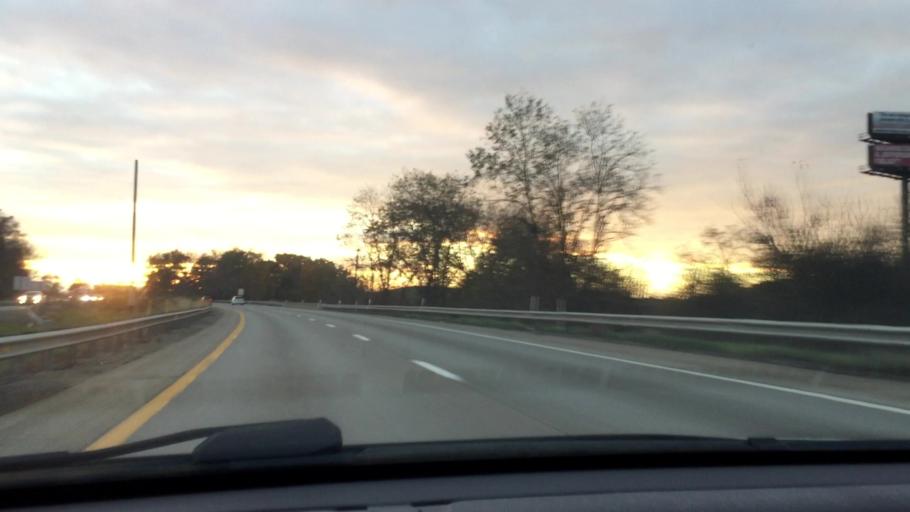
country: US
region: Pennsylvania
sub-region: Washington County
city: McGovern
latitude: 40.2112
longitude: -80.2377
